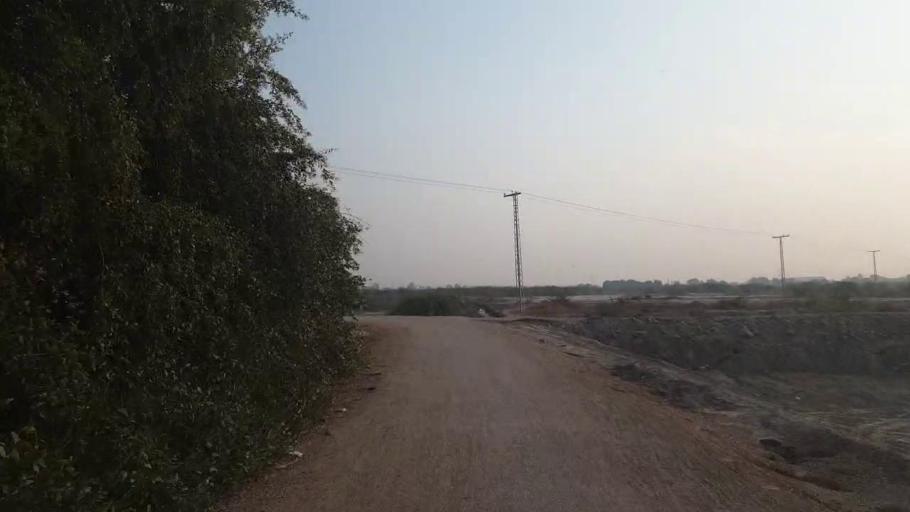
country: PK
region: Sindh
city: Bhit Shah
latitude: 25.7944
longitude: 68.4679
